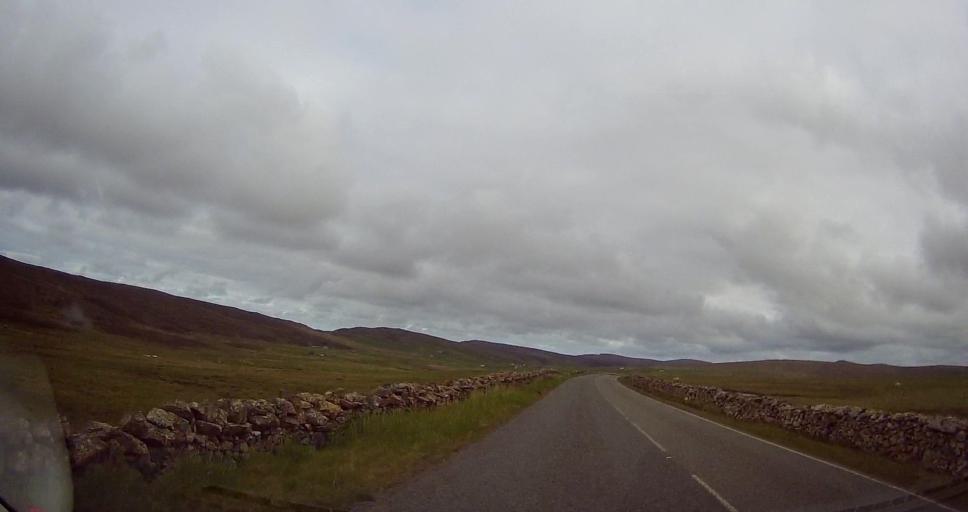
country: GB
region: Scotland
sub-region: Shetland Islands
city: Shetland
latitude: 60.7468
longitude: -0.8848
